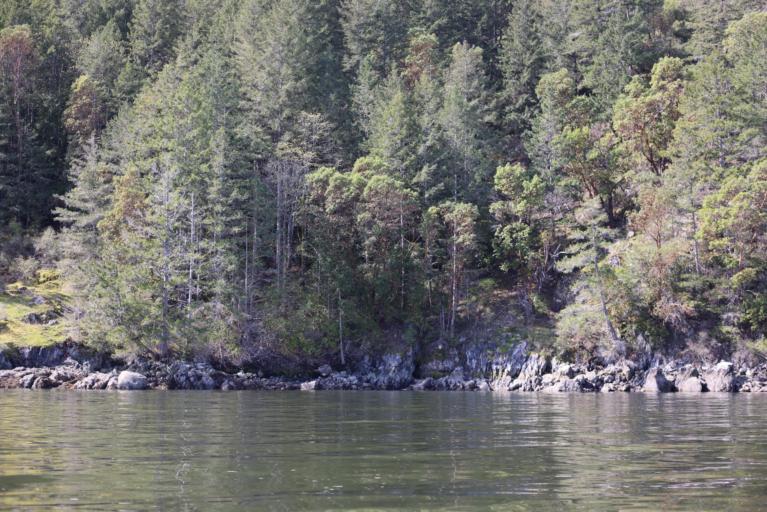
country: CA
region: British Columbia
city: Langford
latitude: 48.5785
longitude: -123.5182
